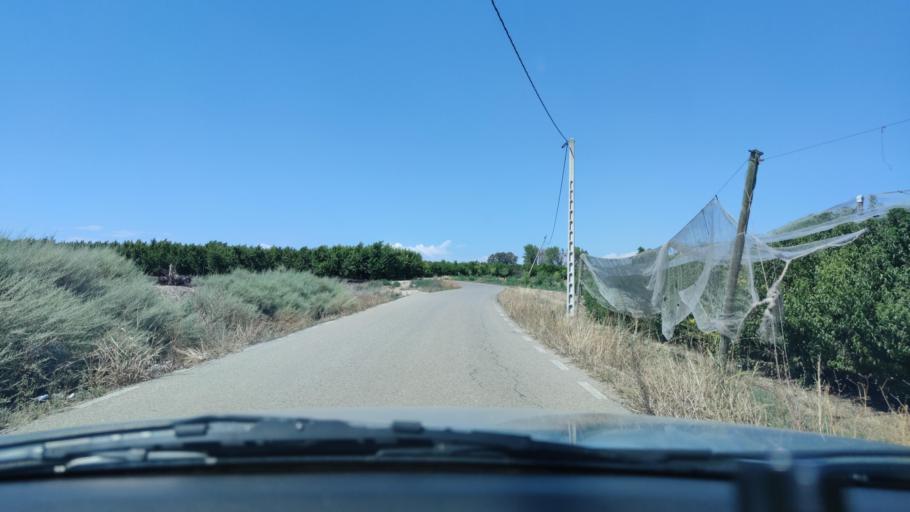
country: ES
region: Catalonia
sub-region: Provincia de Lleida
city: Torrefarrera
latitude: 41.6870
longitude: 0.6214
